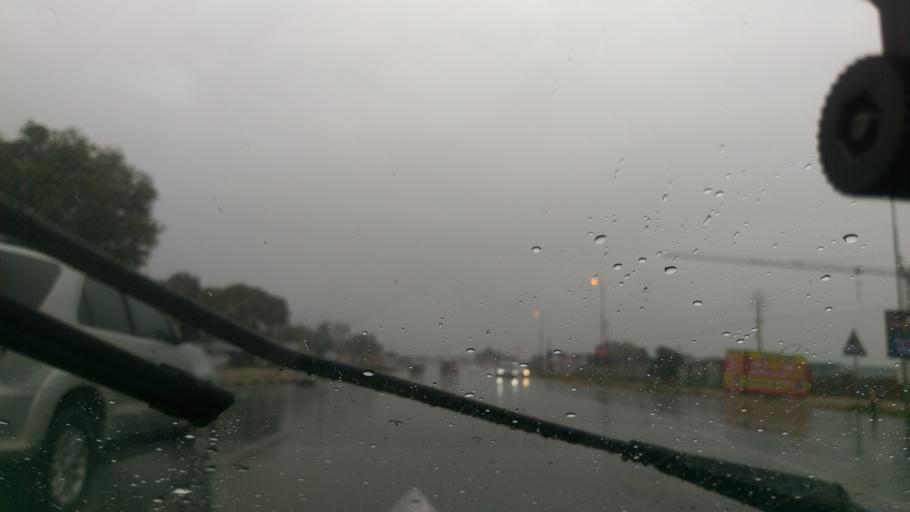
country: ZA
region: Gauteng
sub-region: City of Johannesburg Metropolitan Municipality
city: Diepsloot
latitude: -26.0405
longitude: 27.9583
